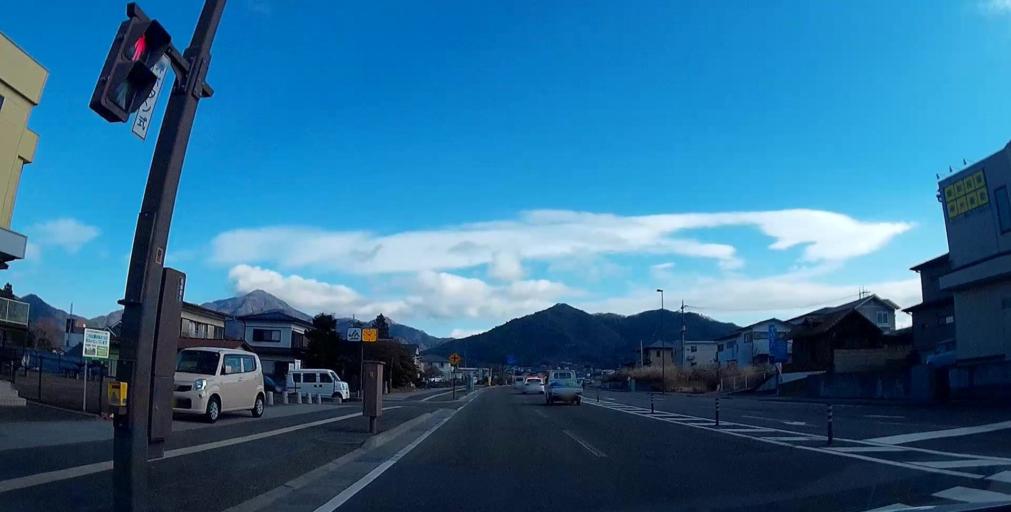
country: JP
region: Yamanashi
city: Fujikawaguchiko
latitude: 35.4854
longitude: 138.8028
